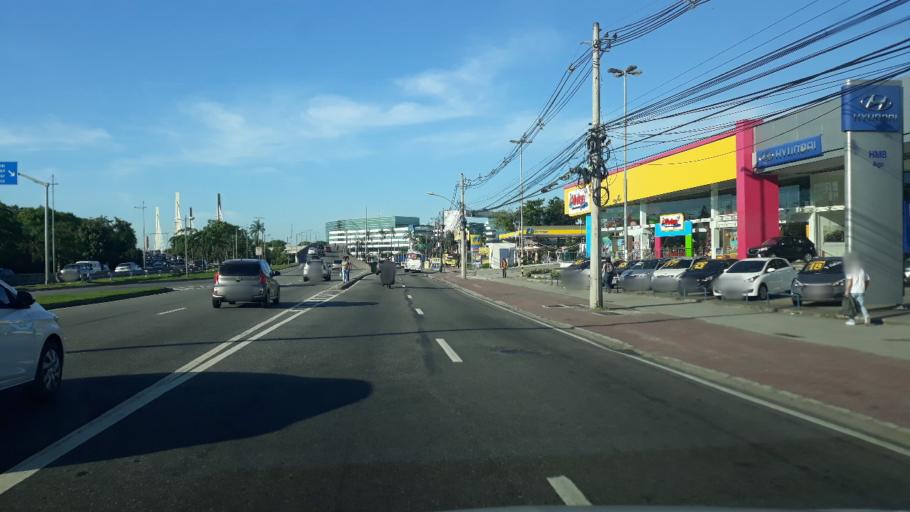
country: BR
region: Rio de Janeiro
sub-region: Sao Joao De Meriti
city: Sao Joao de Meriti
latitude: -22.9716
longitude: -43.3620
